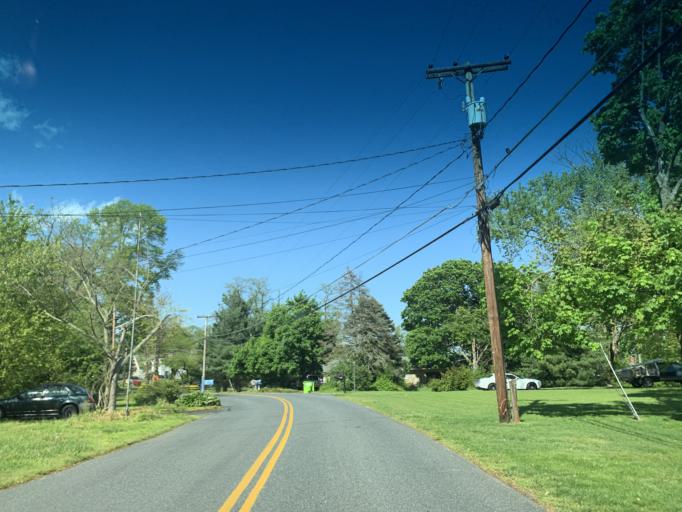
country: US
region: Maryland
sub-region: Harford County
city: Riverside
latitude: 39.4545
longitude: -76.2466
